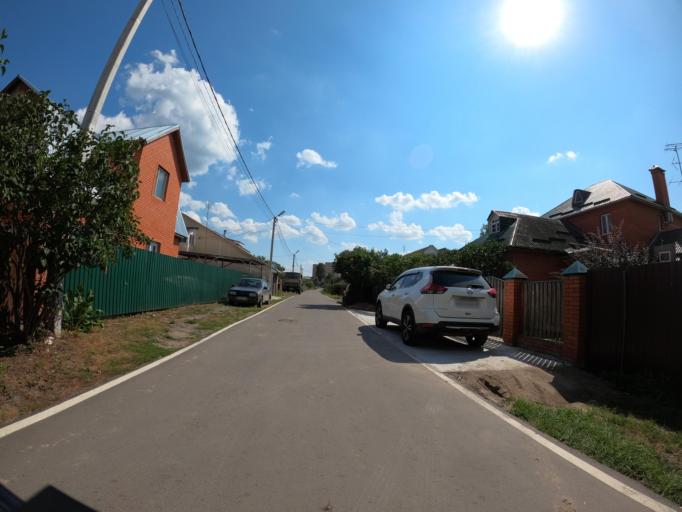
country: RU
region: Moskovskaya
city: Peski
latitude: 55.2555
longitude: 38.7683
